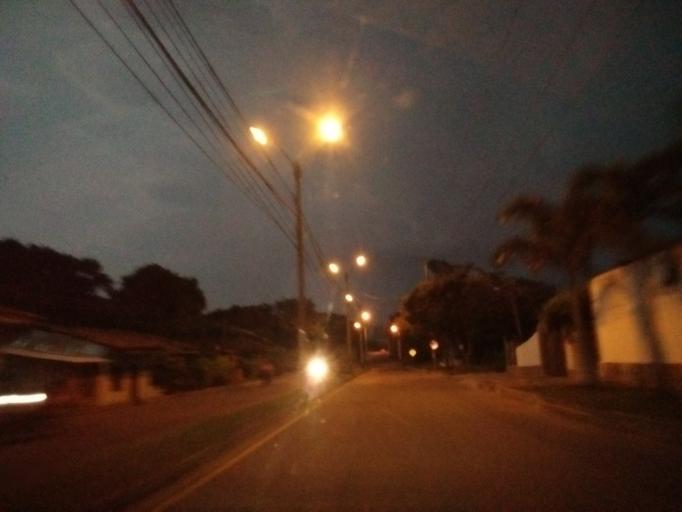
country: CO
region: Cauca
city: Miranda
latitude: 3.2694
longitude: -76.2243
